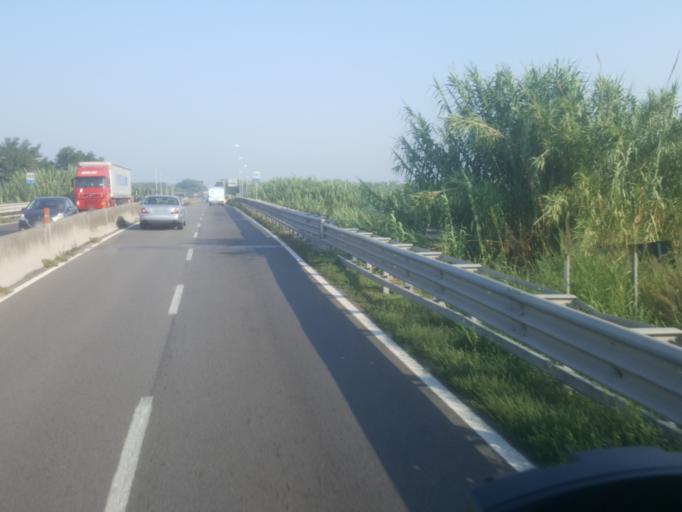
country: IT
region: Emilia-Romagna
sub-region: Provincia di Ravenna
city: Madonna Dell'Albero
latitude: 44.3926
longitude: 12.1855
